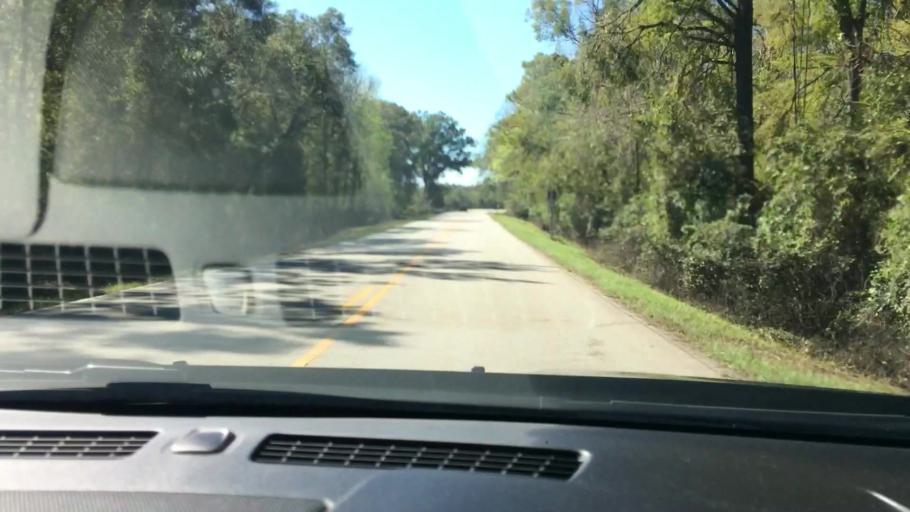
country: US
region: North Carolina
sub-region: Craven County
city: Vanceboro
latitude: 35.3163
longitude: -77.2970
